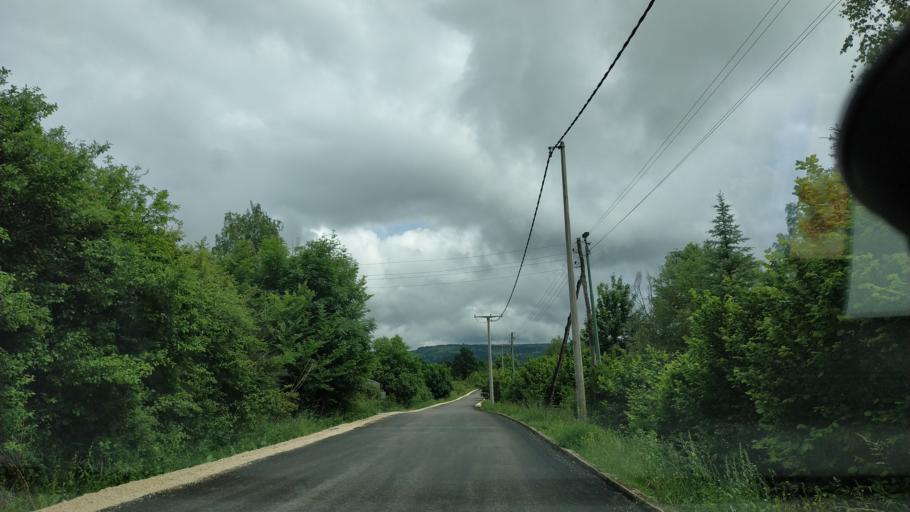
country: RS
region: Central Serbia
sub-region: Zajecarski Okrug
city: Soko Banja
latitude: 43.6501
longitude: 21.9011
